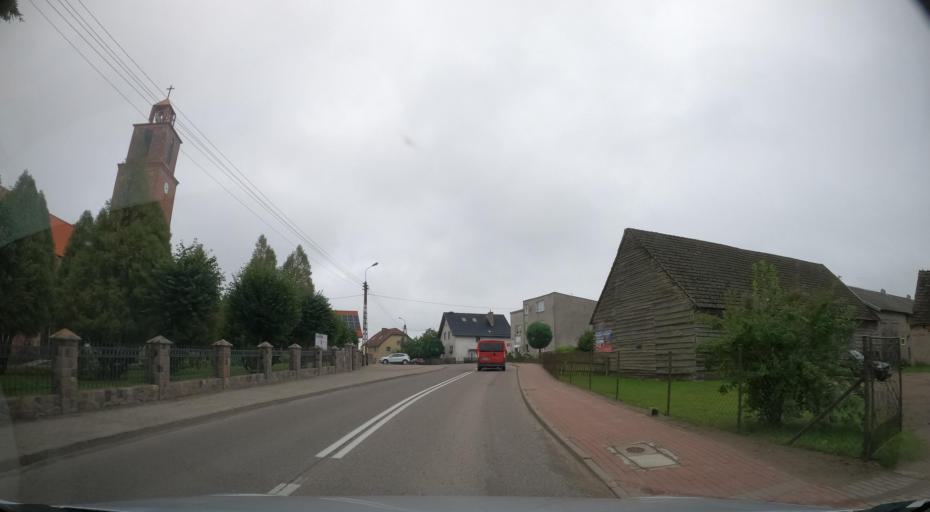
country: PL
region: Pomeranian Voivodeship
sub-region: Powiat wejherowski
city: Linia
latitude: 54.4557
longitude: 18.0237
